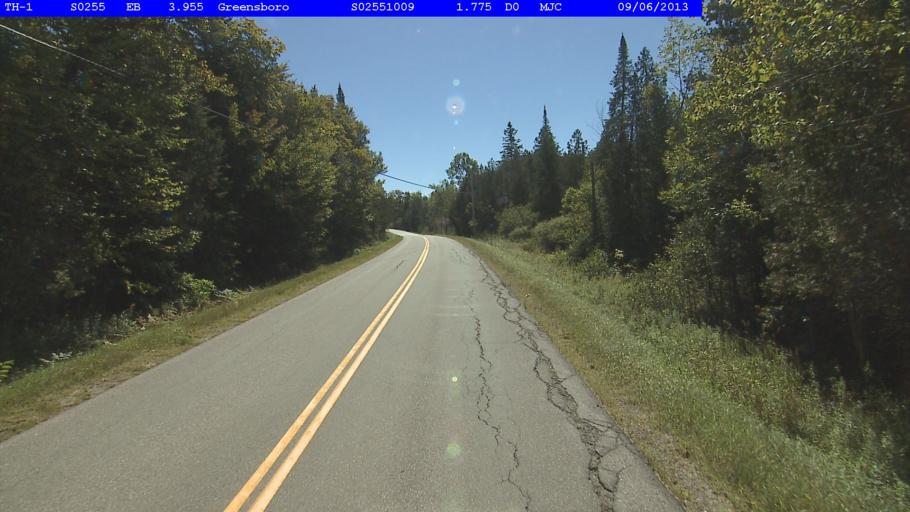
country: US
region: Vermont
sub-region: Caledonia County
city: Hardwick
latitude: 44.6160
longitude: -72.3257
